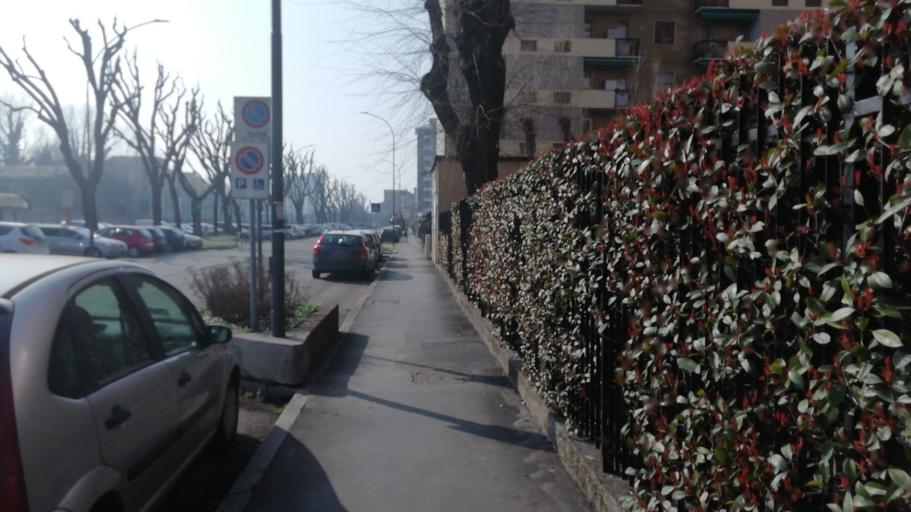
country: IT
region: Lombardy
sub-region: Citta metropolitana di Milano
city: Romano Banco
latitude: 45.4375
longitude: 9.1126
